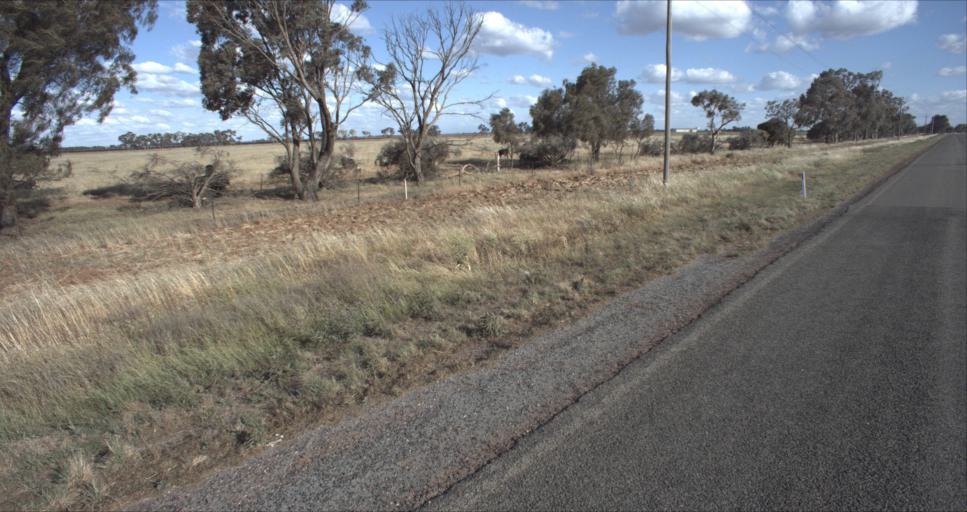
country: AU
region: New South Wales
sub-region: Leeton
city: Leeton
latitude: -34.5333
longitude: 146.2810
